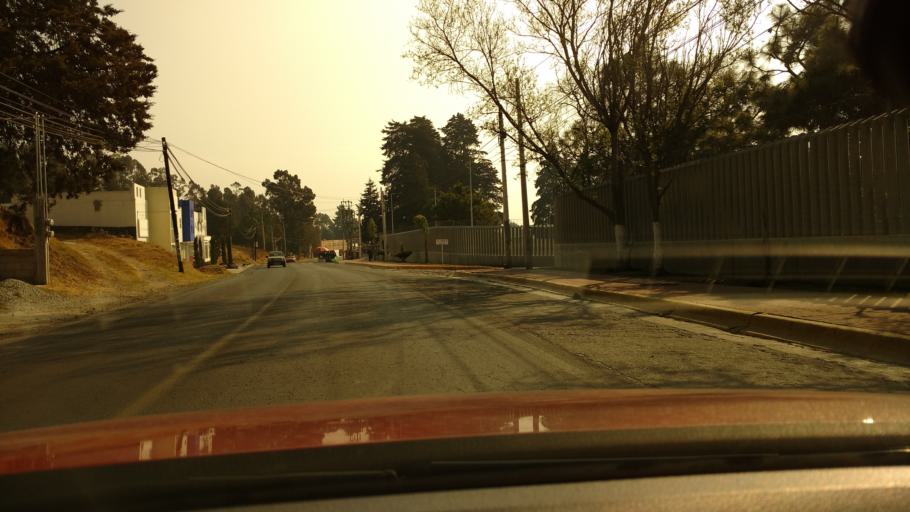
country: MX
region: Morelos
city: Chapultepec
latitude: 19.2032
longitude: -99.5560
